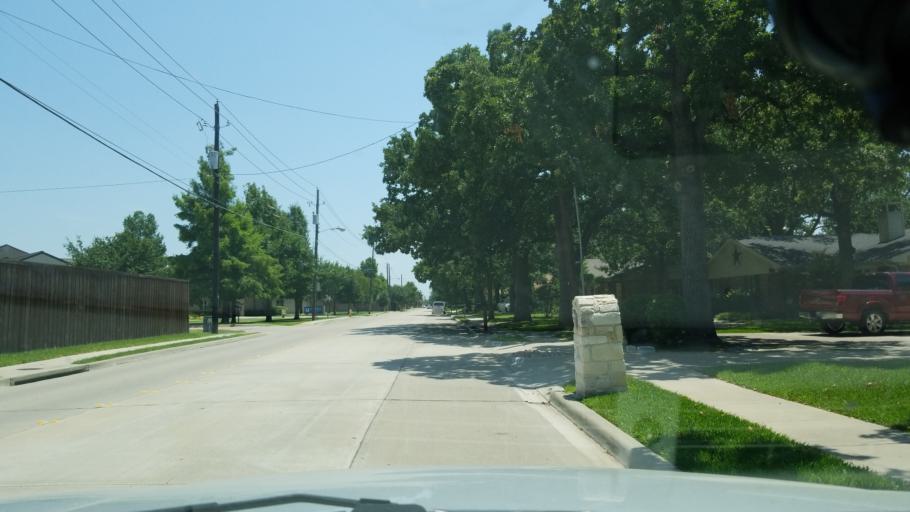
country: US
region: Texas
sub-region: Dallas County
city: Coppell
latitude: 32.9683
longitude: -96.9891
